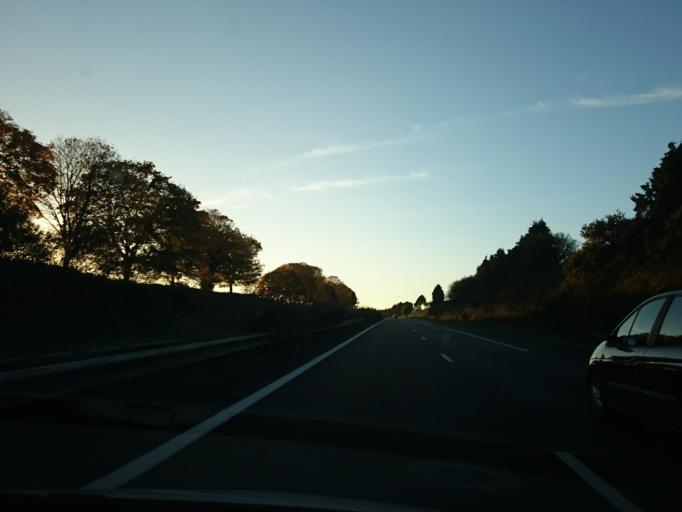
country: FR
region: Brittany
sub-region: Departement du Finistere
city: Saint-Thegonnec
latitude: 48.5266
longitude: -3.9718
